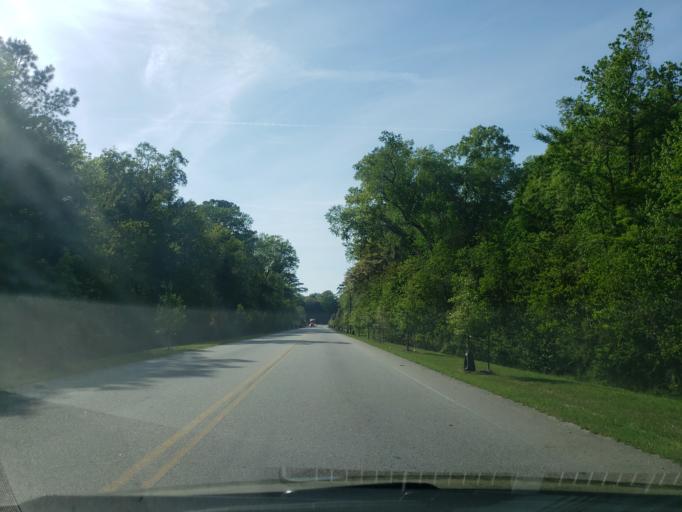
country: US
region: Georgia
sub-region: Chatham County
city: Garden City
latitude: 32.1034
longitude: -81.1918
